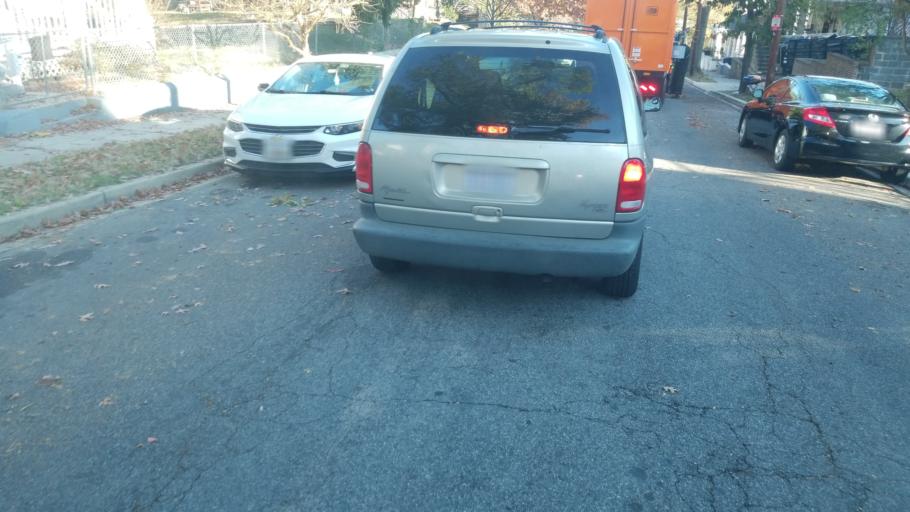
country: US
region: Maryland
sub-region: Prince George's County
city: Capitol Heights
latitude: 38.8929
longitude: -76.9194
